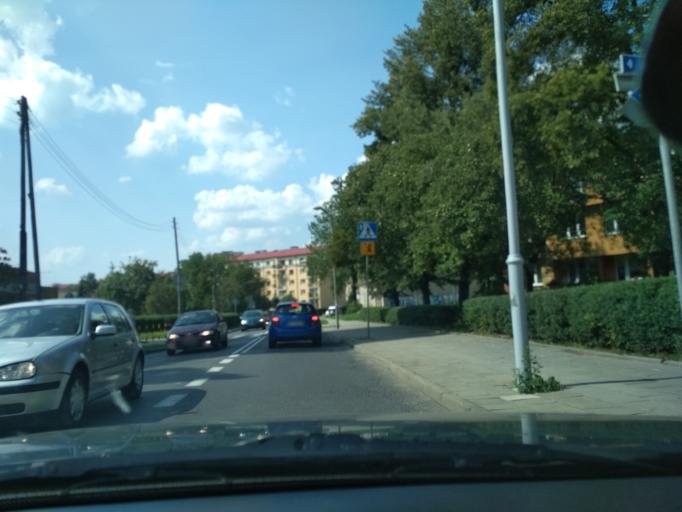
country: PL
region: Silesian Voivodeship
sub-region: Gliwice
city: Gliwice
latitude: 50.2828
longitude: 18.6762
